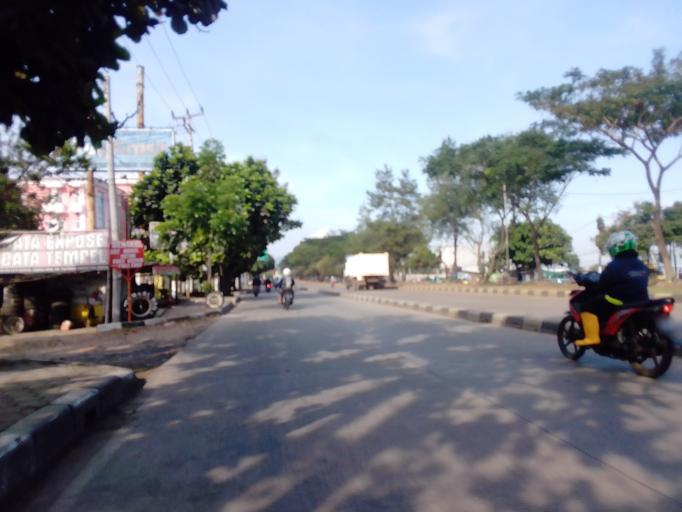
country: ID
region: West Java
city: Cileunyi
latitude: -6.9353
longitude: 107.7145
